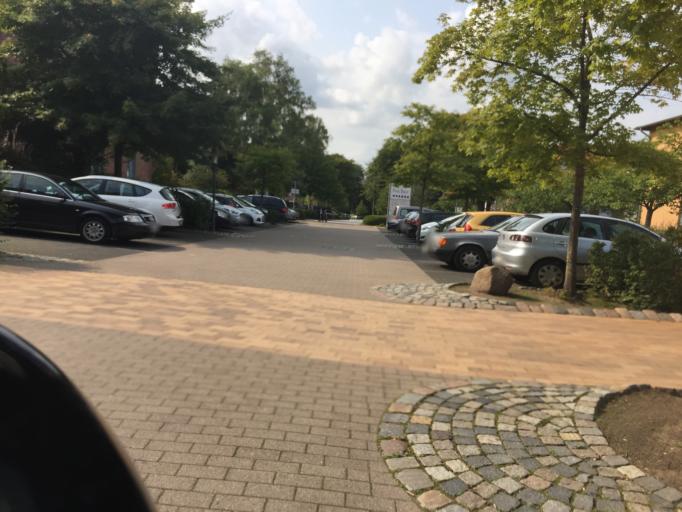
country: DE
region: Schleswig-Holstein
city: Itzehoe
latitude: 53.9321
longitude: 9.5230
